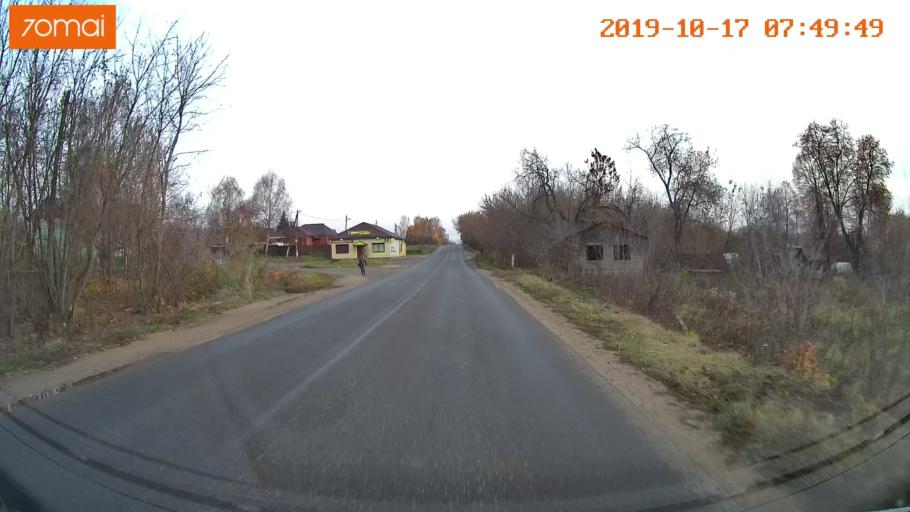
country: RU
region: Vladimir
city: Yur'yev-Pol'skiy
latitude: 56.4801
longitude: 39.6655
